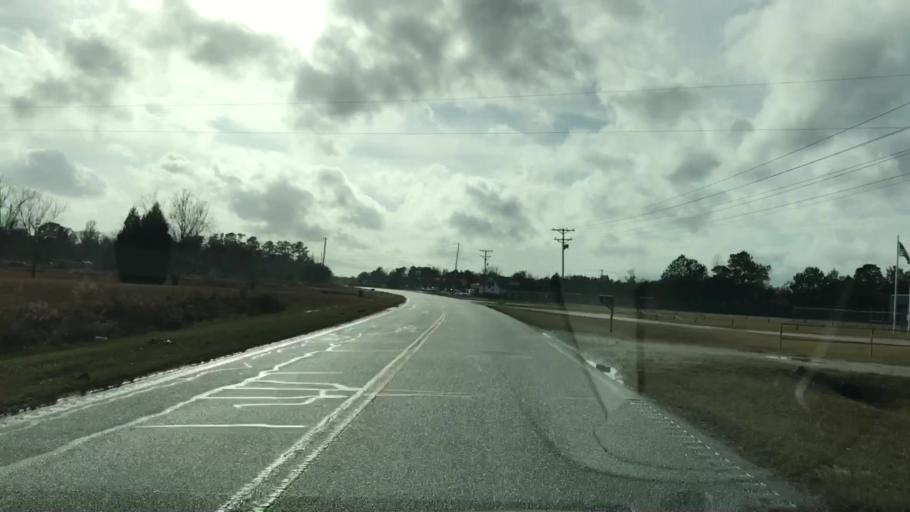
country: US
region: South Carolina
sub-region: Williamsburg County
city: Andrews
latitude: 33.4962
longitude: -79.5394
